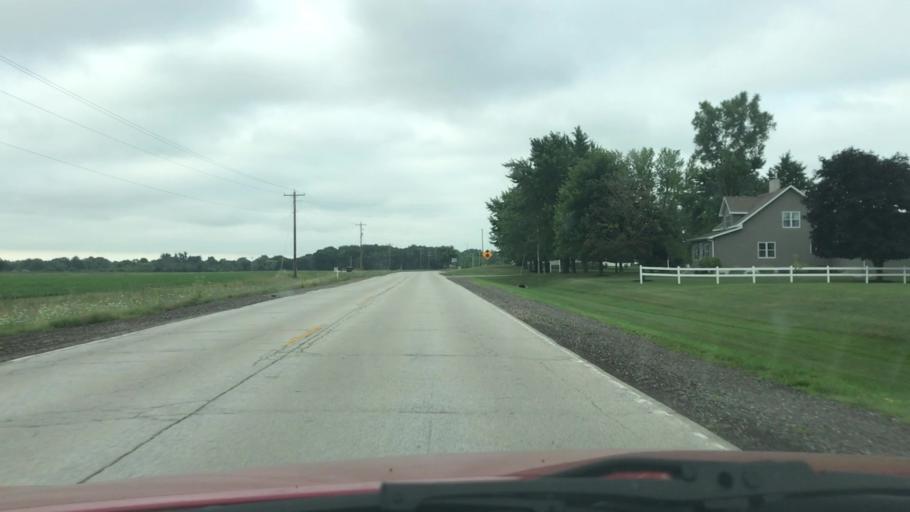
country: US
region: Wisconsin
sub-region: Brown County
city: De Pere
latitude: 44.4339
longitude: -88.1359
